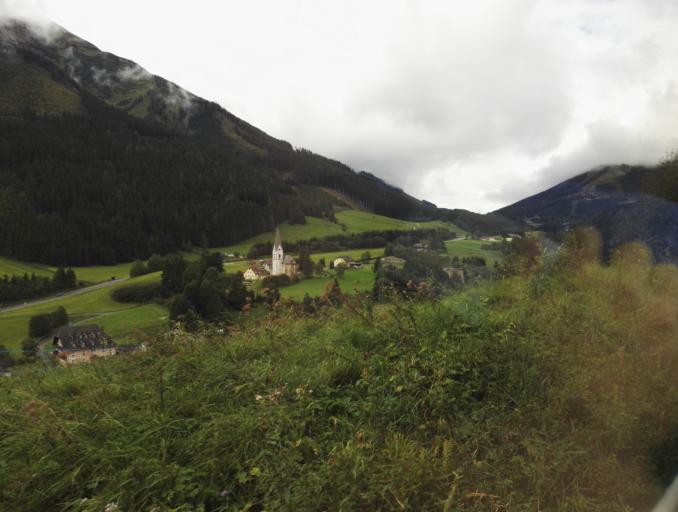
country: AT
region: Styria
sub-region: Politischer Bezirk Leoben
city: Vordernberg
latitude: 47.4995
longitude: 14.9924
